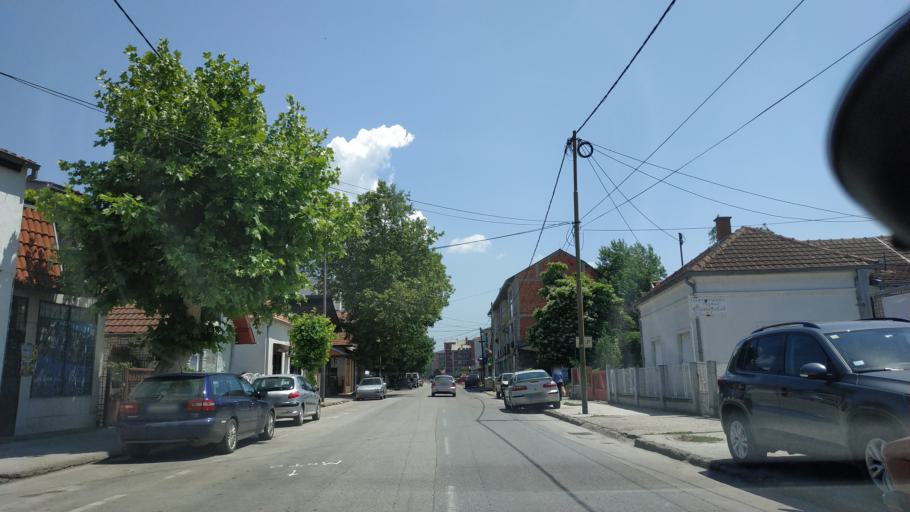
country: RS
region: Central Serbia
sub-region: Pomoravski Okrug
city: Cuprija
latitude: 43.9341
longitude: 21.3761
